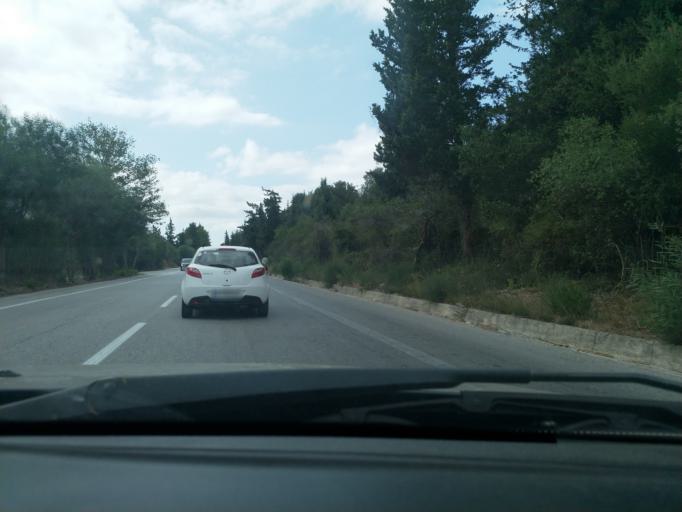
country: GR
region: Crete
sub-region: Nomos Chanias
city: Kalivai
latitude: 35.3880
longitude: 24.1829
